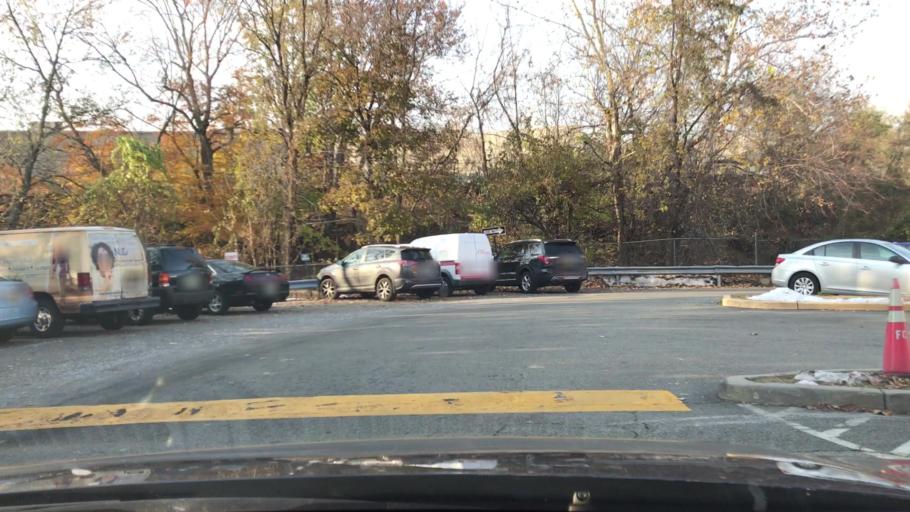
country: US
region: New Jersey
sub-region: Bergen County
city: Hasbrouck Heights
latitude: 40.8669
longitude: -74.0968
